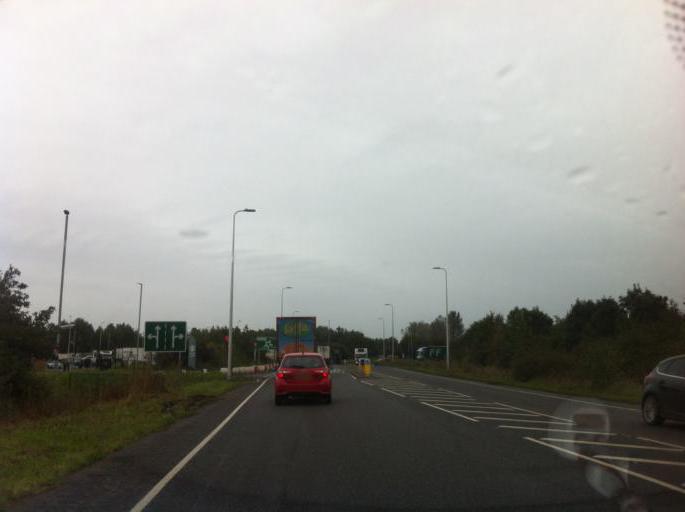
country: GB
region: England
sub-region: Lincolnshire
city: Kirton
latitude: 52.8884
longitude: -0.0850
